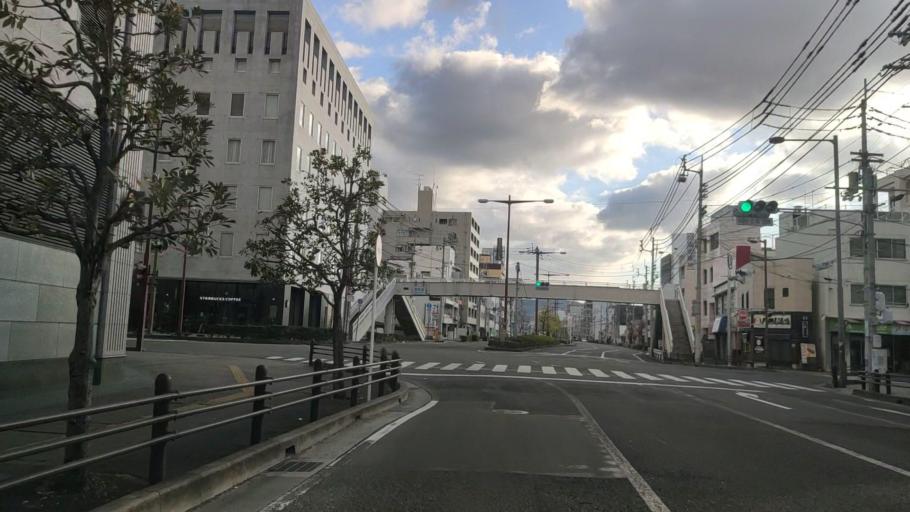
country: JP
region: Ehime
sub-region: Shikoku-chuo Shi
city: Matsuyama
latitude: 33.8355
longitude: 132.7634
